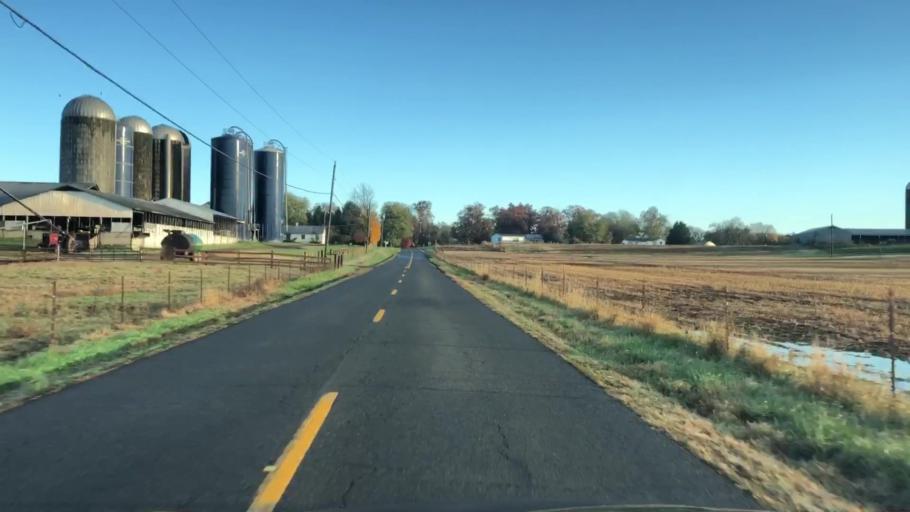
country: US
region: Virginia
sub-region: Prince William County
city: Nokesville
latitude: 38.6761
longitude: -77.6696
